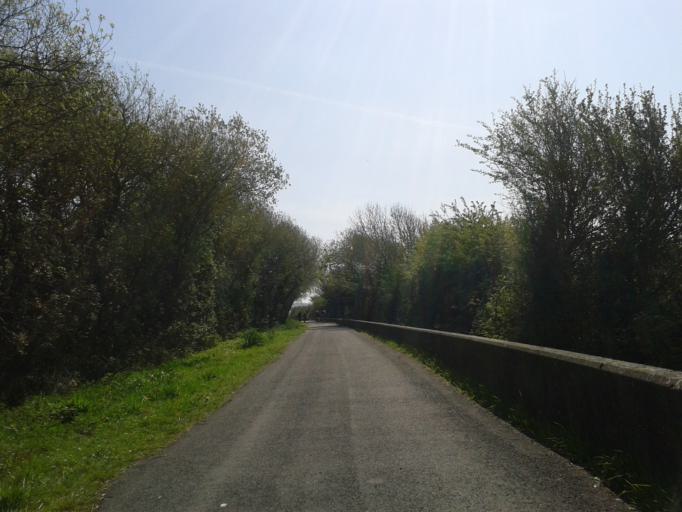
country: GB
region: England
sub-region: Devon
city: Barnstaple
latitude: 51.0850
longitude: -4.0862
